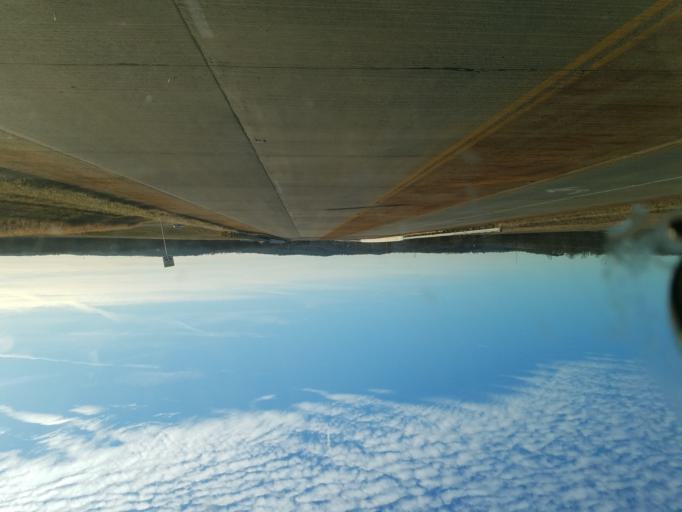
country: US
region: Ohio
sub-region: Muskingum County
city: Frazeysburg
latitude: 40.1382
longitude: -82.0989
